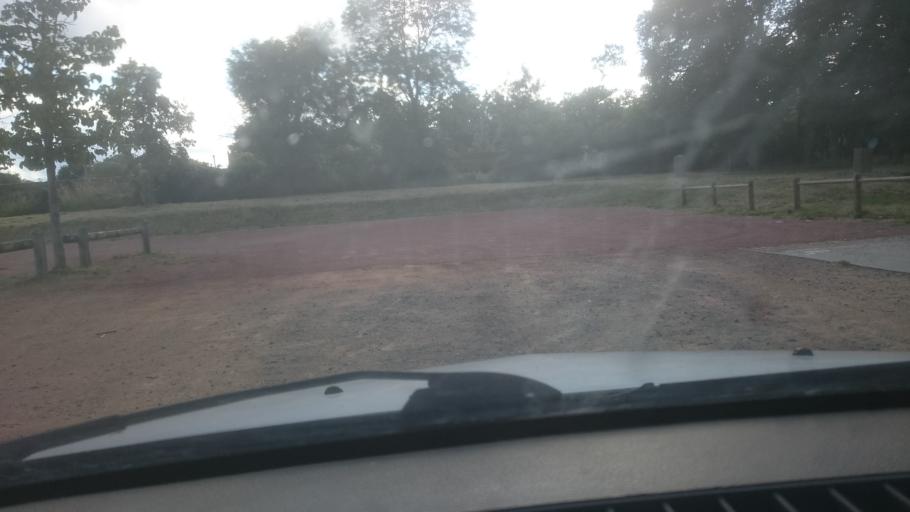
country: FR
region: Rhone-Alpes
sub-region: Departement du Rhone
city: Saint-Verand
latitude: 45.9071
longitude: 4.5690
